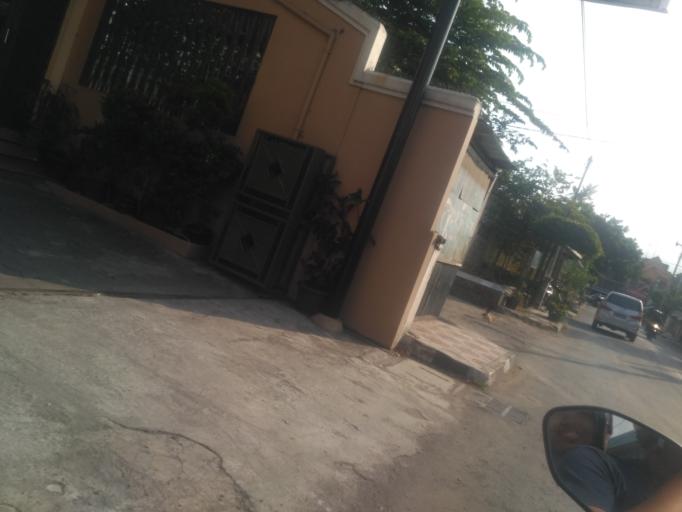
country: ID
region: Daerah Istimewa Yogyakarta
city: Yogyakarta
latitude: -7.7976
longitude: 110.3574
